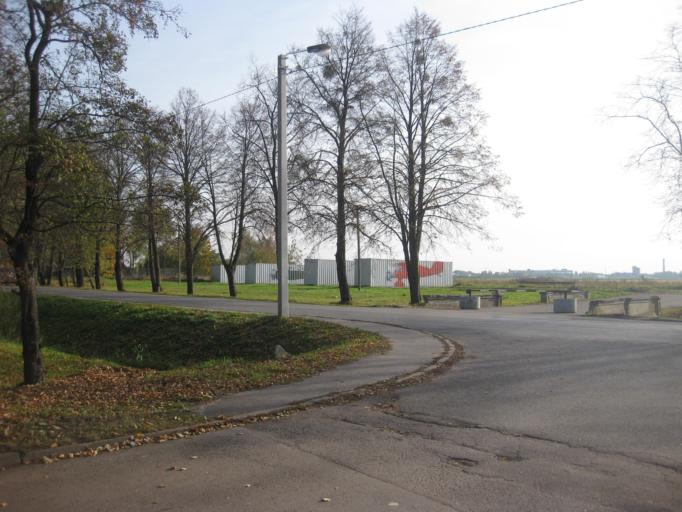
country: LT
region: Kauno apskritis
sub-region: Kaunas
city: Aleksotas
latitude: 54.8896
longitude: 23.8831
